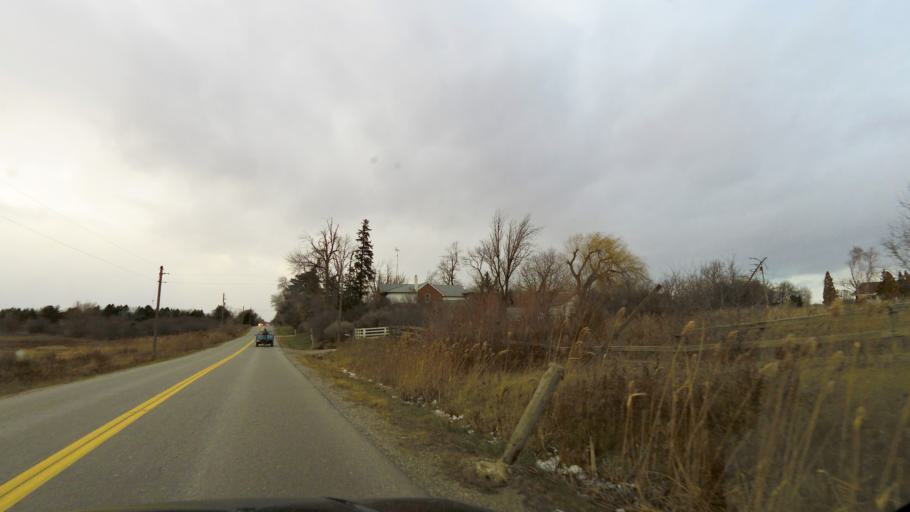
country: CA
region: Ontario
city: Brampton
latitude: 43.8109
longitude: -79.6919
